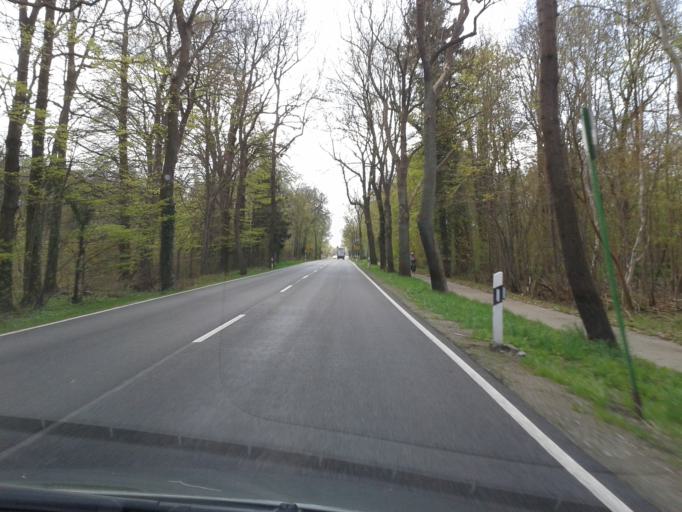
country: DE
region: Lower Saxony
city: Lubbow
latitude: 52.8904
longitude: 11.1771
